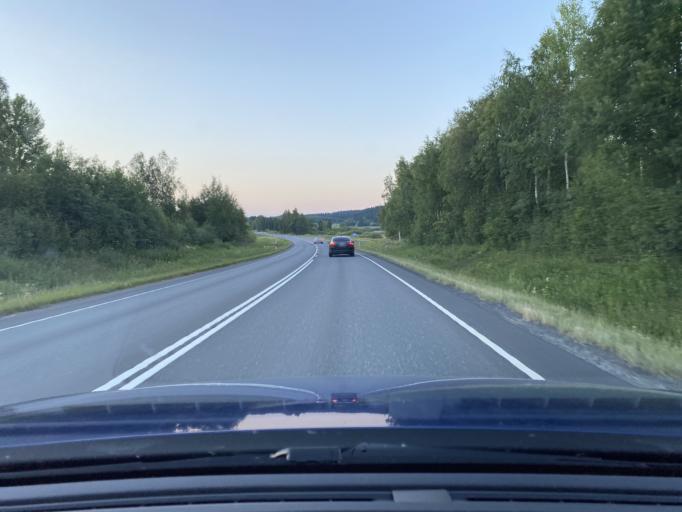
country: FI
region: Pirkanmaa
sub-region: Luoteis-Pirkanmaa
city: Ikaalinen
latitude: 61.8645
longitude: 22.9602
